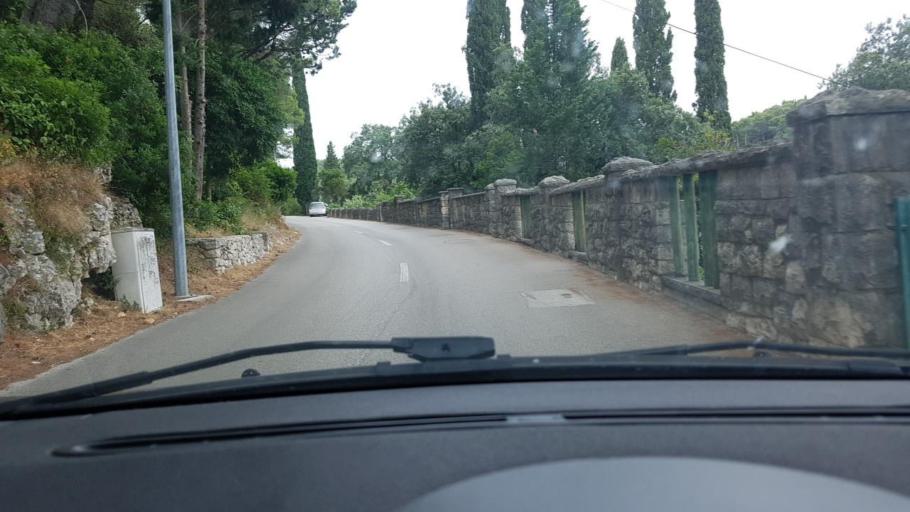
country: HR
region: Dubrovacko-Neretvanska
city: Korcula
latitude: 42.9615
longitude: 17.1278
